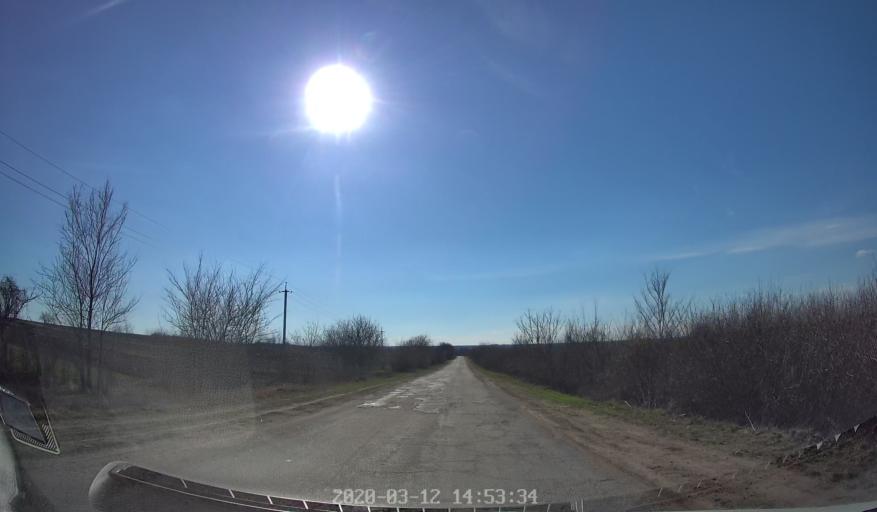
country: MD
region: Criuleni
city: Criuleni
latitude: 47.2175
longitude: 29.0780
